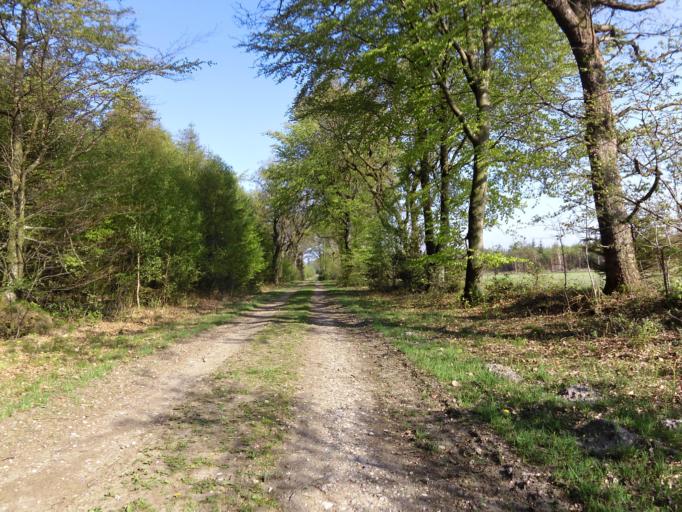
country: DK
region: South Denmark
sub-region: Tonder Kommune
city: Toftlund
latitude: 55.1961
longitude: 8.9387
